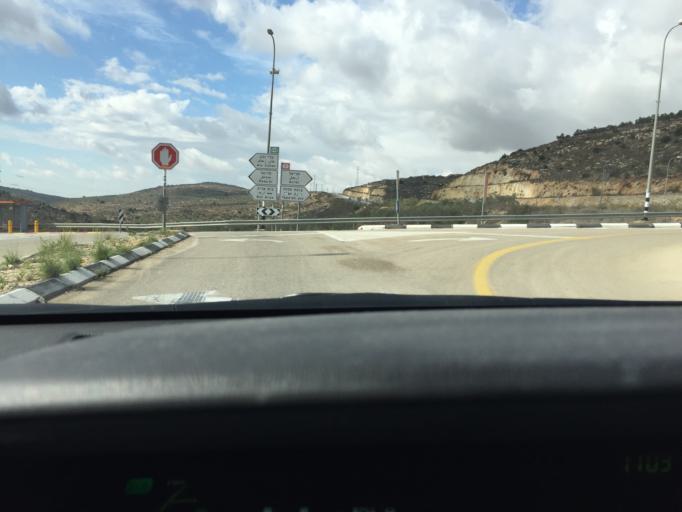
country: PS
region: West Bank
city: Sartah
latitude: 32.0922
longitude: 35.1044
